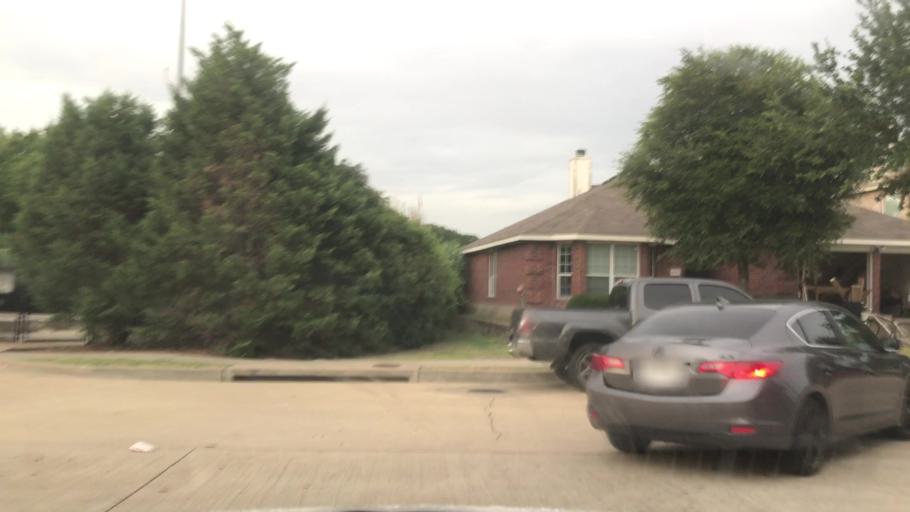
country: US
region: Texas
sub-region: Kaufman County
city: Forney
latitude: 32.7213
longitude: -96.5372
